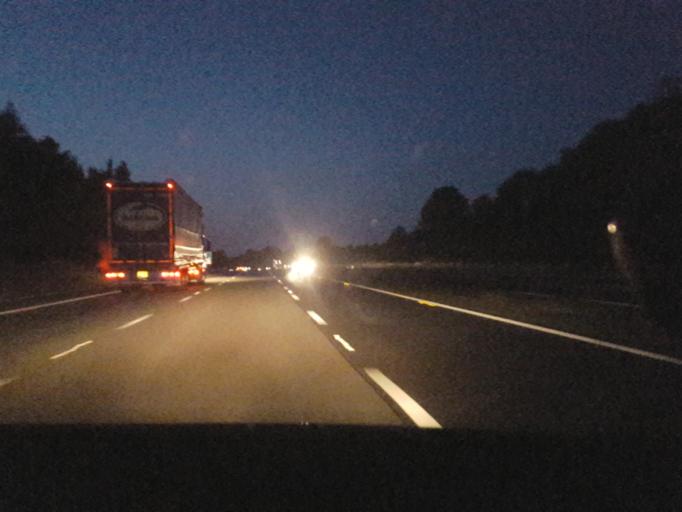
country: GB
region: England
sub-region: Leicestershire
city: Shepshed
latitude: 52.7396
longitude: -1.2802
